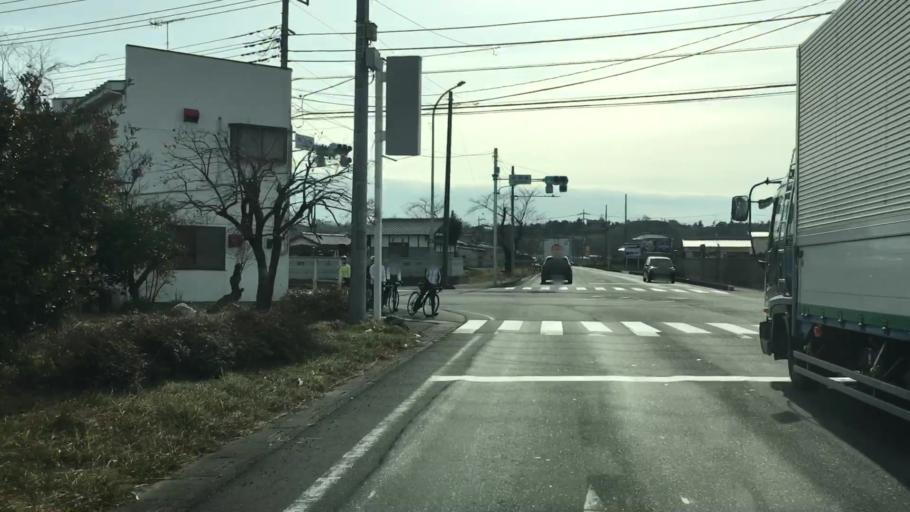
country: JP
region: Saitama
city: Kumagaya
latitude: 36.1314
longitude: 139.3239
